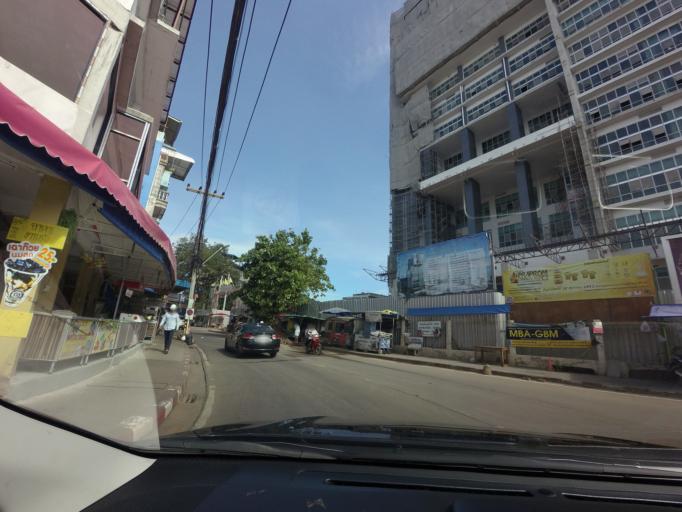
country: TH
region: Chon Buri
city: Si Racha
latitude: 13.1609
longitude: 100.9192
